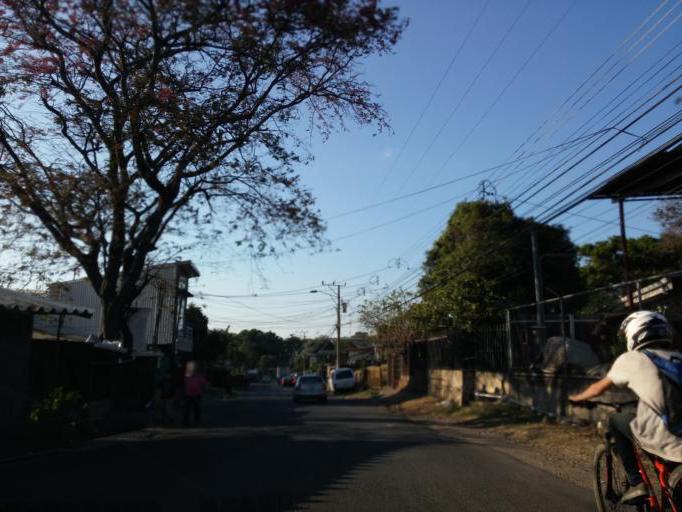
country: CR
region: Heredia
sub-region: Canton de Belen
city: San Antonio
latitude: 9.9747
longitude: -84.2230
